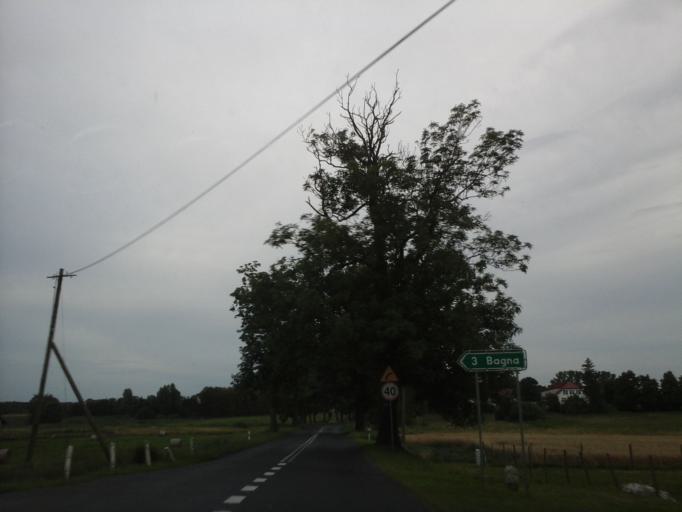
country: PL
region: West Pomeranian Voivodeship
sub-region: Powiat goleniowski
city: Maszewo
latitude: 53.5409
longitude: 15.1229
